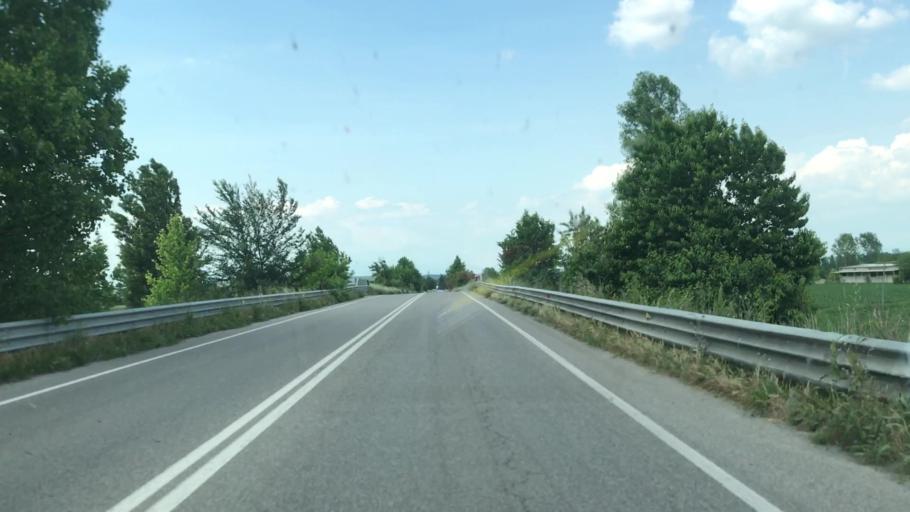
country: IT
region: Lombardy
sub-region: Provincia di Mantova
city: Castel Goffredo
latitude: 45.2997
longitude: 10.4918
